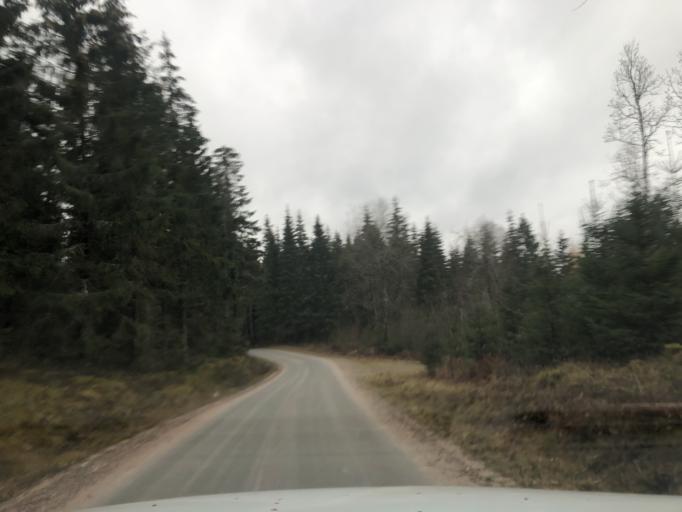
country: SE
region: Vaestra Goetaland
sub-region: Ulricehamns Kommun
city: Ulricehamn
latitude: 57.8745
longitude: 13.5616
